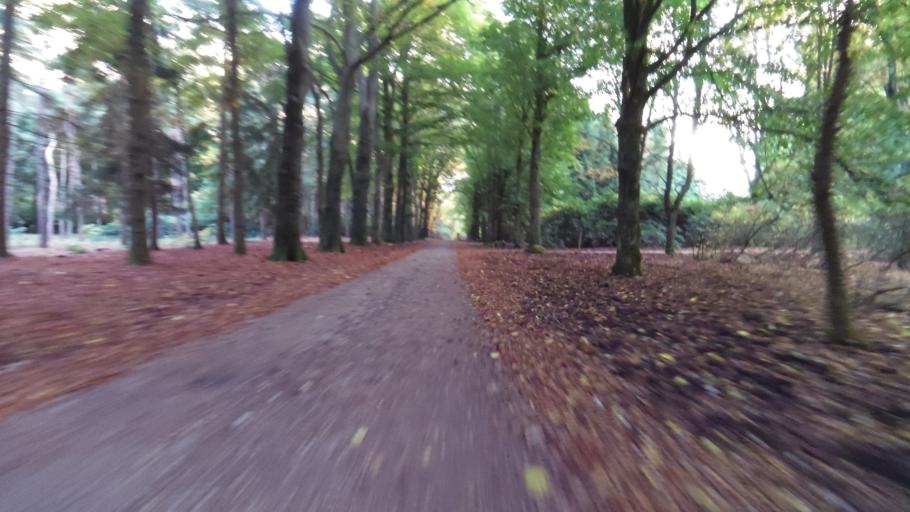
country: NL
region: Gelderland
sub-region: Gemeente Ede
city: Wekerom
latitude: 52.0817
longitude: 5.7008
